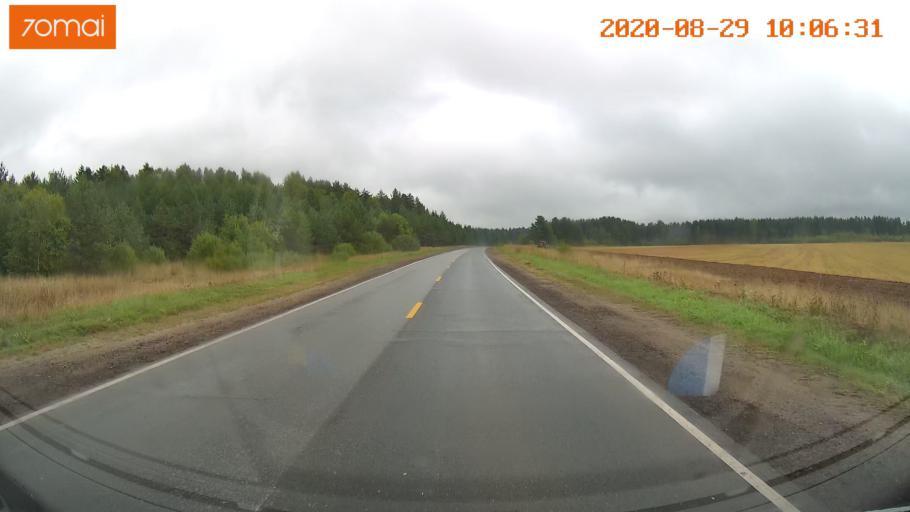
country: RU
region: Ivanovo
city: Kuznechikha
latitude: 57.3881
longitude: 42.5472
